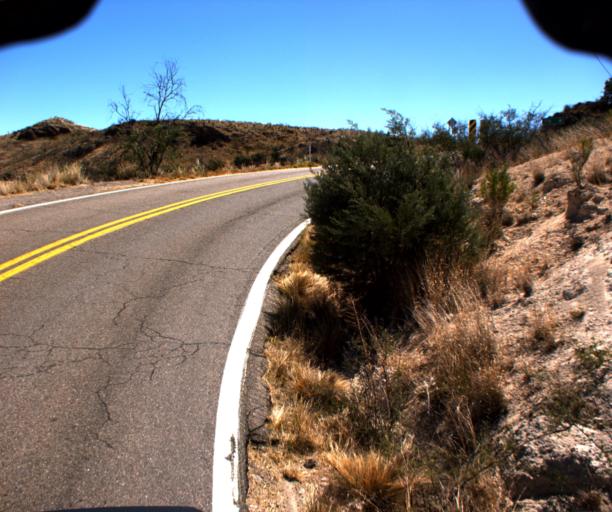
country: US
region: Arizona
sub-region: Santa Cruz County
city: Rio Rico
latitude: 31.3956
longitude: -111.0874
